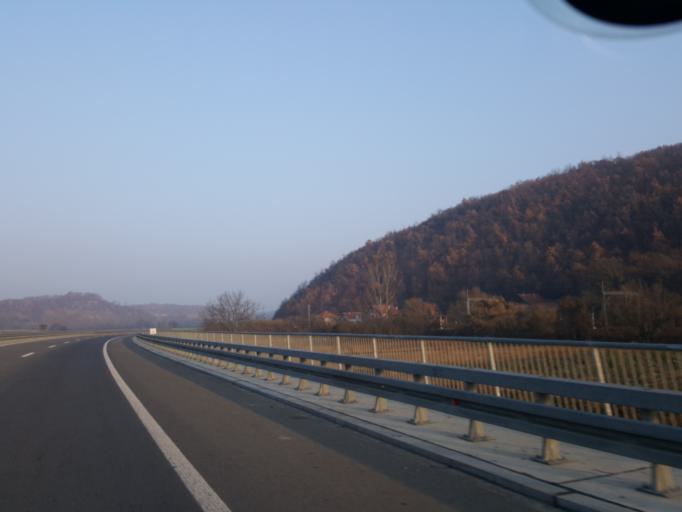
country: RS
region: Central Serbia
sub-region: Jablanicki Okrug
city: Vlasotince
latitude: 42.8950
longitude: 22.0548
